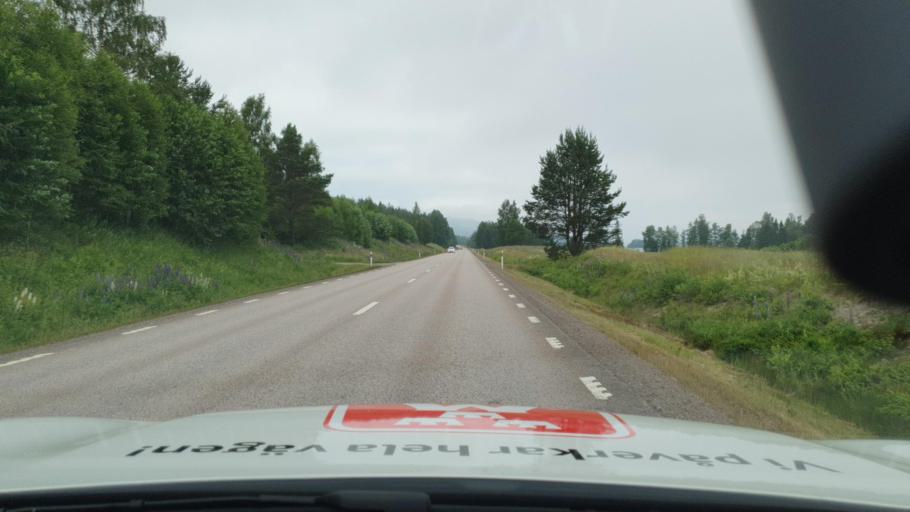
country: SE
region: Vaermland
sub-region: Sunne Kommun
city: Sunne
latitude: 59.9318
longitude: 13.1257
